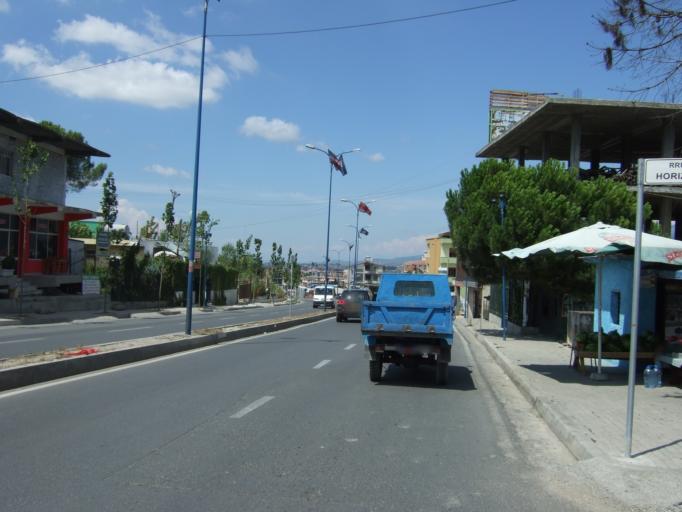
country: AL
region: Tirane
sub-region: Rrethi i Tiranes
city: Kamez
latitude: 41.3625
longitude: 19.7719
